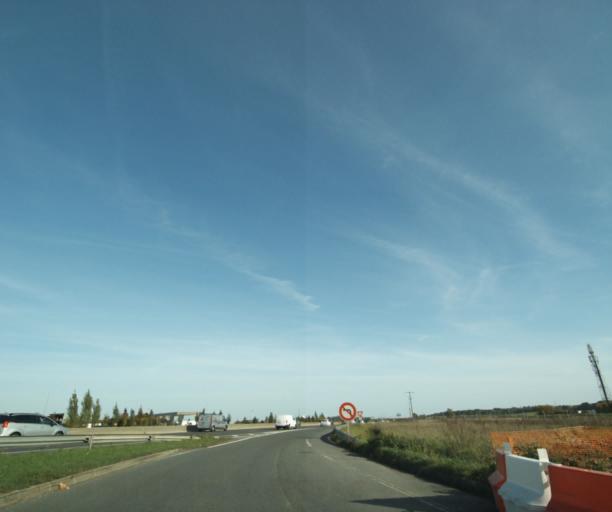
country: FR
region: Ile-de-France
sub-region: Departement de Seine-et-Marne
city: Chanteloup-en-Brie
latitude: 48.8293
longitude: 2.7443
